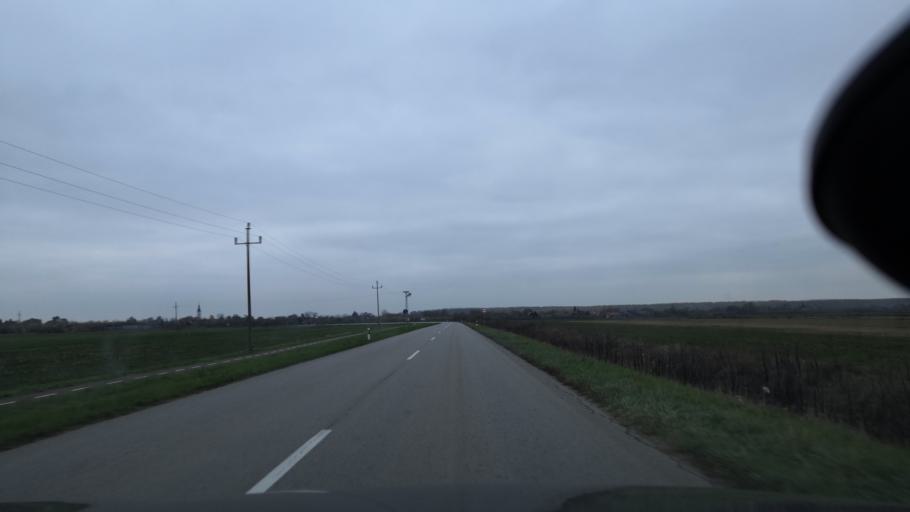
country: HU
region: Csongrad
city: Roszke
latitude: 46.1360
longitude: 20.0942
